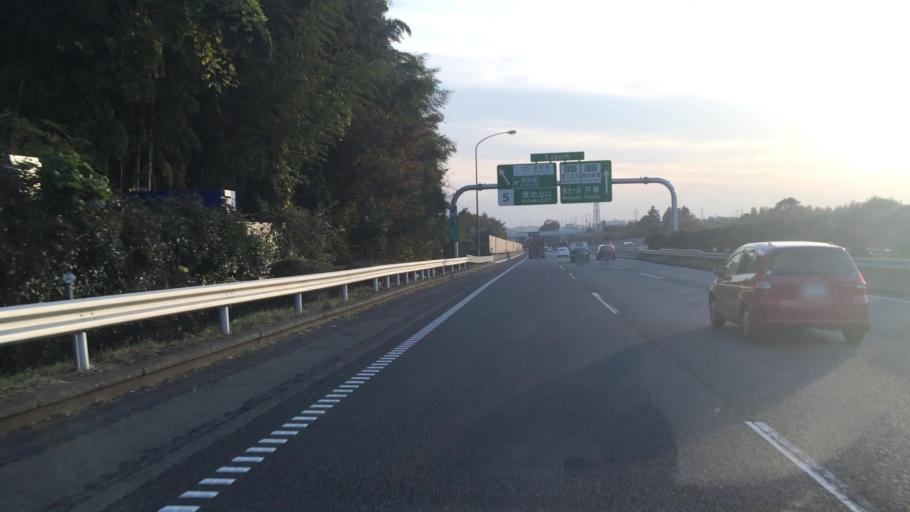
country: JP
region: Kanagawa
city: Yokohama
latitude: 35.5304
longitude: 139.5984
